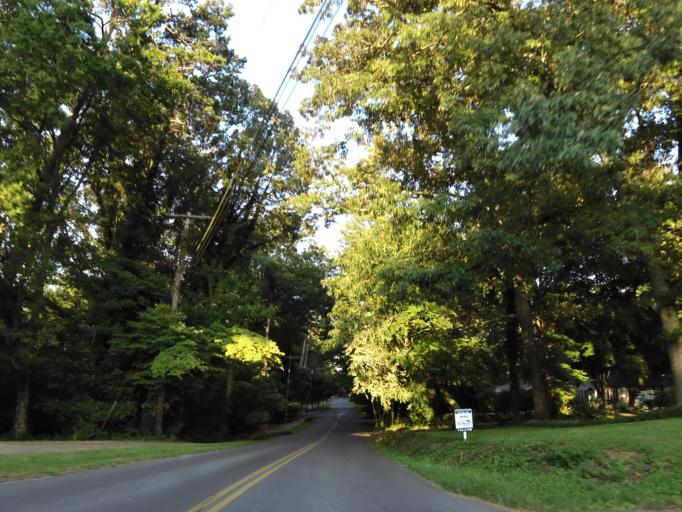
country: US
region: Tennessee
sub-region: McMinn County
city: Athens
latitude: 35.4559
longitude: -84.5909
